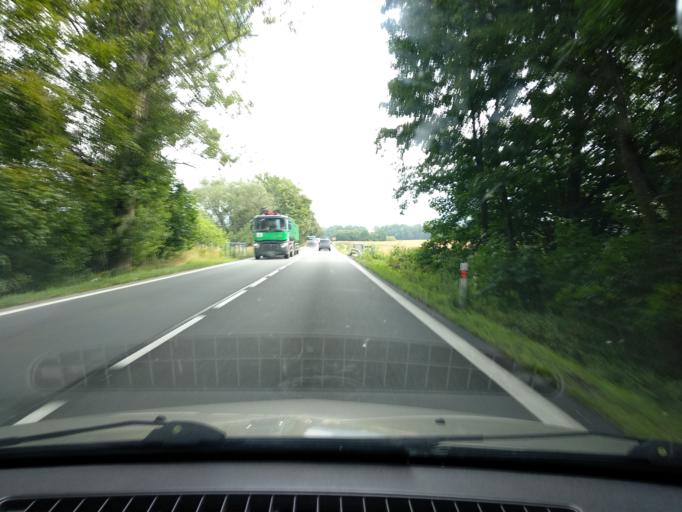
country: CZ
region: Olomoucky
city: Postrelmov
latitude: 49.9194
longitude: 16.9180
